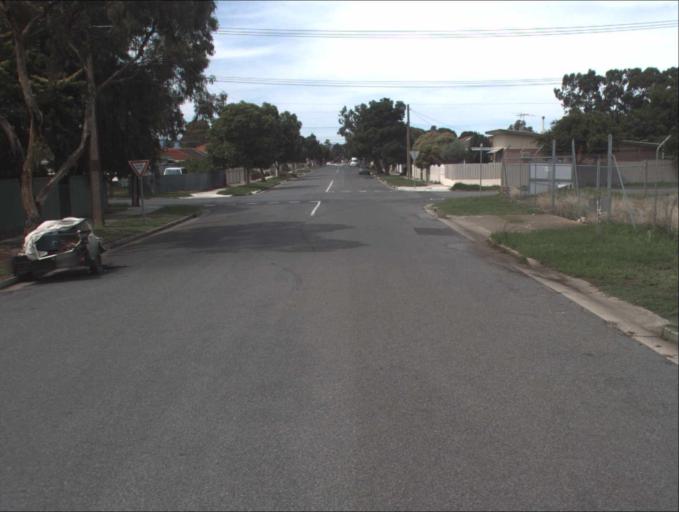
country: AU
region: South Australia
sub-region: Port Adelaide Enfield
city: Alberton
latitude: -34.8451
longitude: 138.5294
